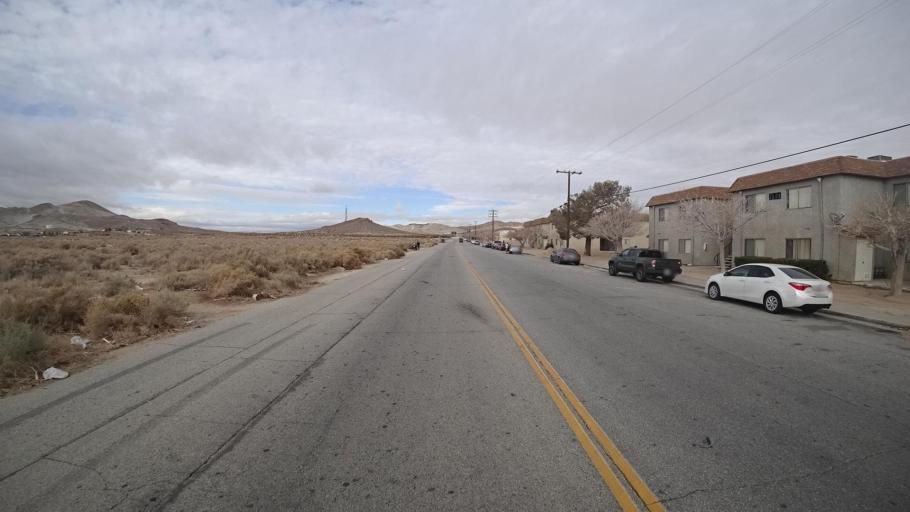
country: US
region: California
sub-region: Kern County
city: Rosamond
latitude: 34.8692
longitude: -118.1586
